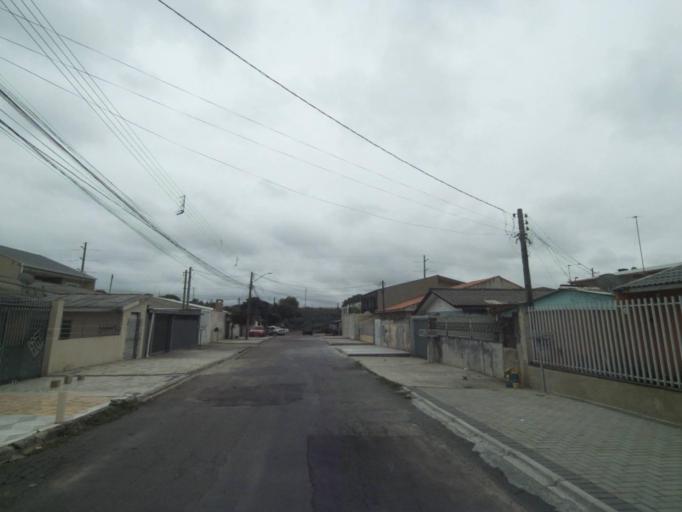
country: BR
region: Parana
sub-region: Araucaria
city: Araucaria
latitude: -25.5275
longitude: -49.3376
